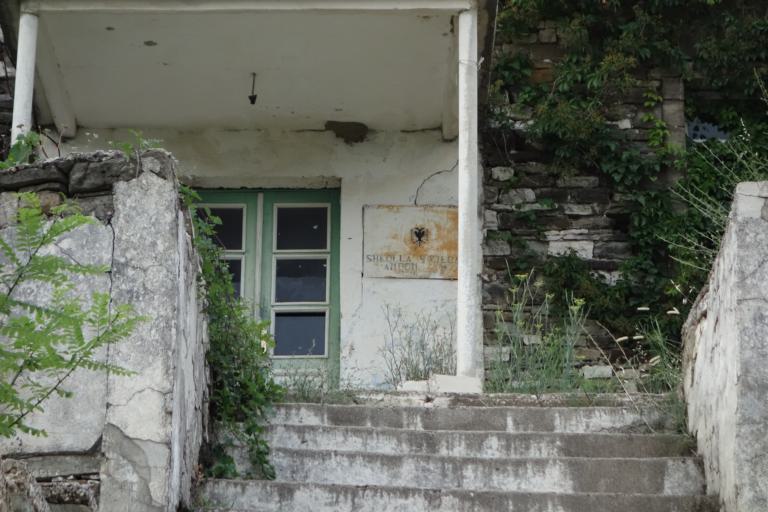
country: AL
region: Gjirokaster
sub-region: Rrethi i Gjirokastres
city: Vithkuq
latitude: 40.1696
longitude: 20.3054
